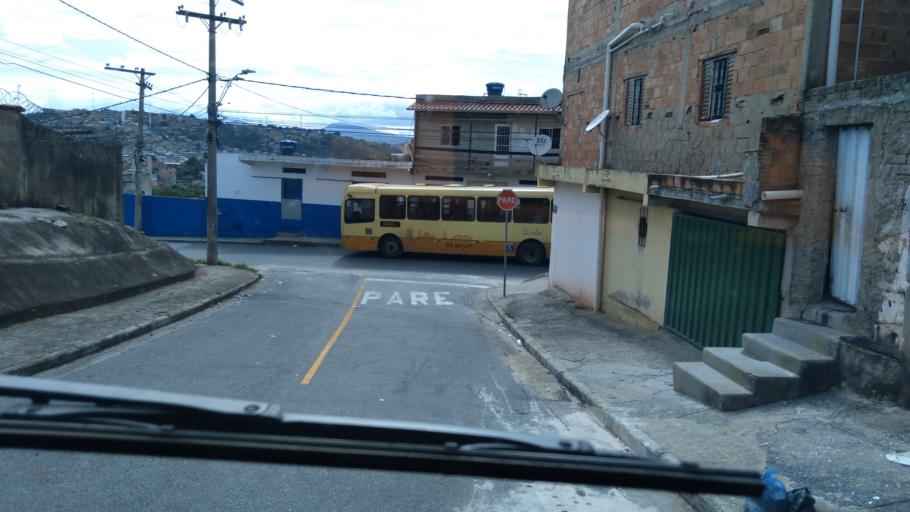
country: BR
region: Minas Gerais
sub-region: Santa Luzia
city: Santa Luzia
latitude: -19.8333
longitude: -43.8976
